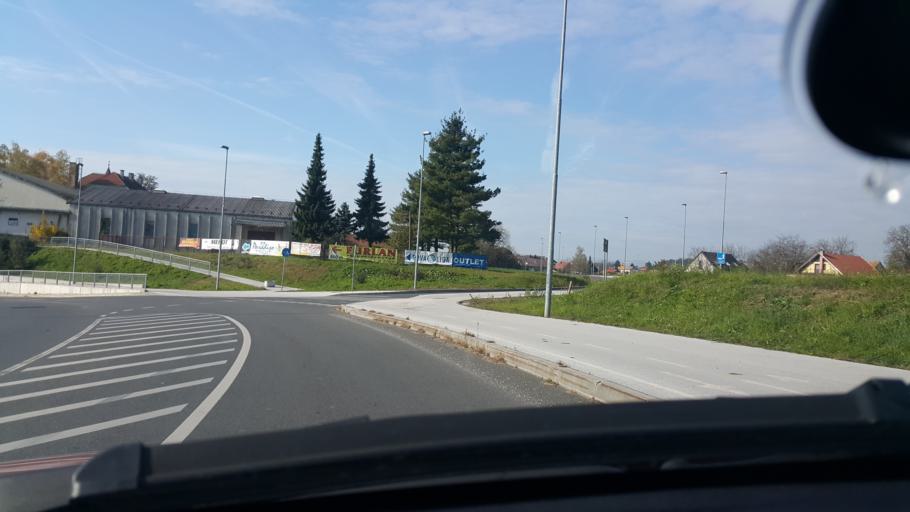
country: HR
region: Zagrebacka
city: Bregana
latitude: 45.8967
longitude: 15.6626
